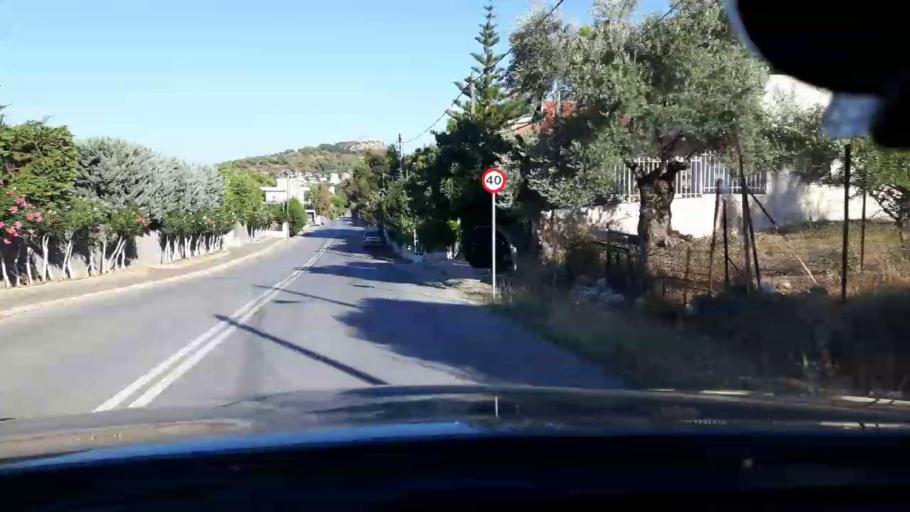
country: GR
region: Attica
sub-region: Nomarchia Anatolikis Attikis
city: Limin Mesoyaias
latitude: 37.8848
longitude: 23.9977
